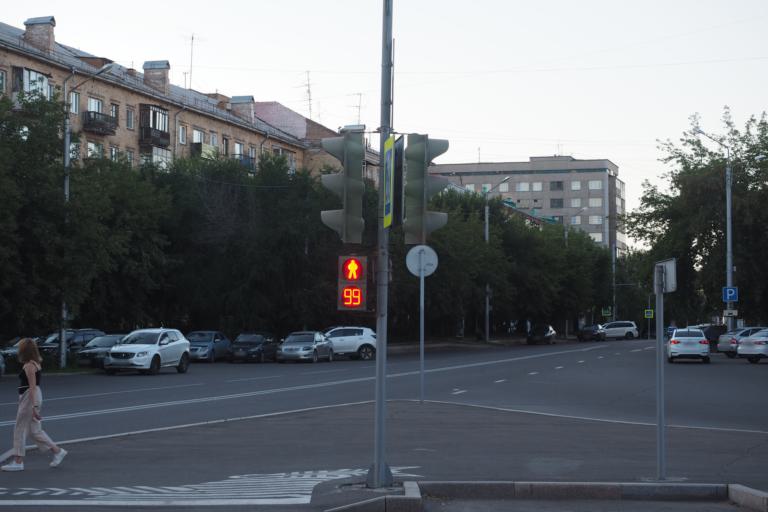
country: RU
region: Krasnoyarskiy
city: Krasnoyarsk
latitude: 56.0080
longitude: 92.8821
